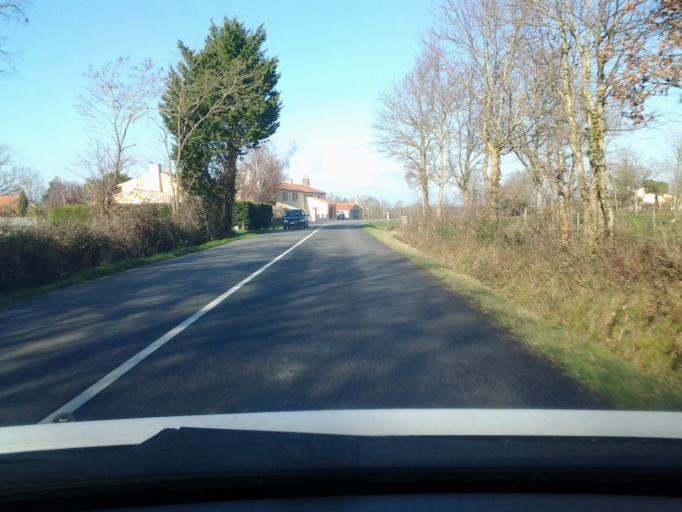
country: FR
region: Pays de la Loire
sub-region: Departement de la Vendee
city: Mouilleron-le-Captif
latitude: 46.7075
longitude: -1.4156
